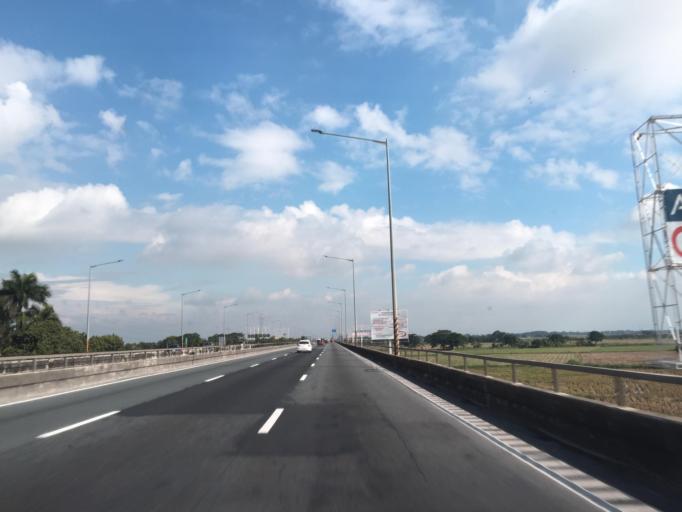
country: PH
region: Central Luzon
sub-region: Province of Pampanga
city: Balucuc
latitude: 14.9346
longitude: 120.7942
